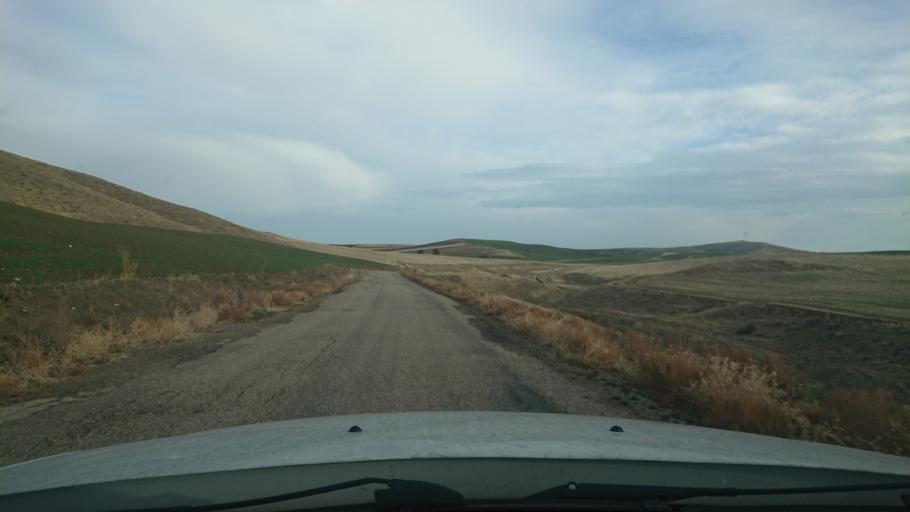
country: TR
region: Aksaray
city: Acipinar
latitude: 38.6411
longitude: 33.8081
